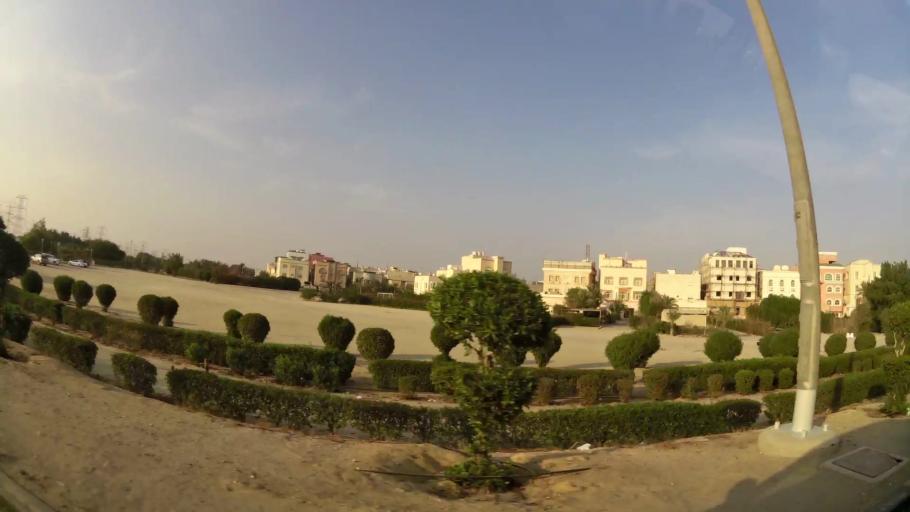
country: KW
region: Mubarak al Kabir
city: Sabah as Salim
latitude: 29.2205
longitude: 48.0572
